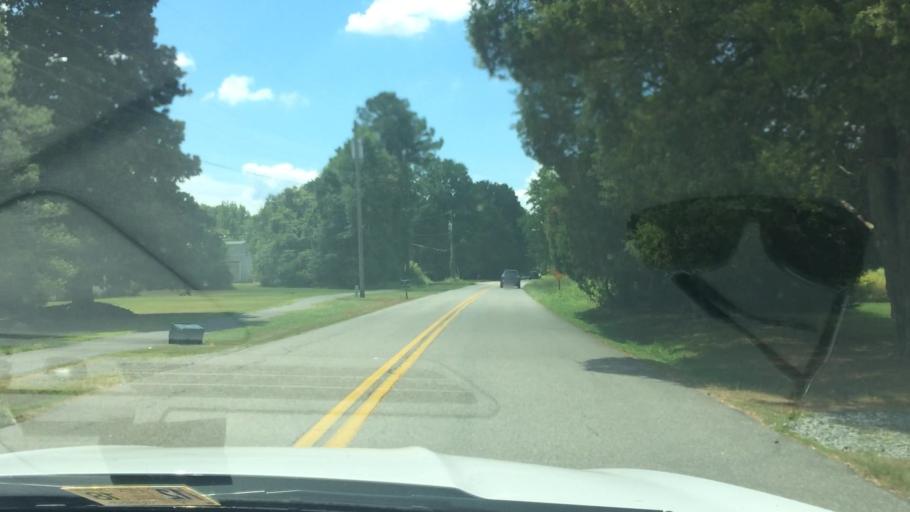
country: US
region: Virginia
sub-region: King William County
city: West Point
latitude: 37.5534
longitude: -76.7933
